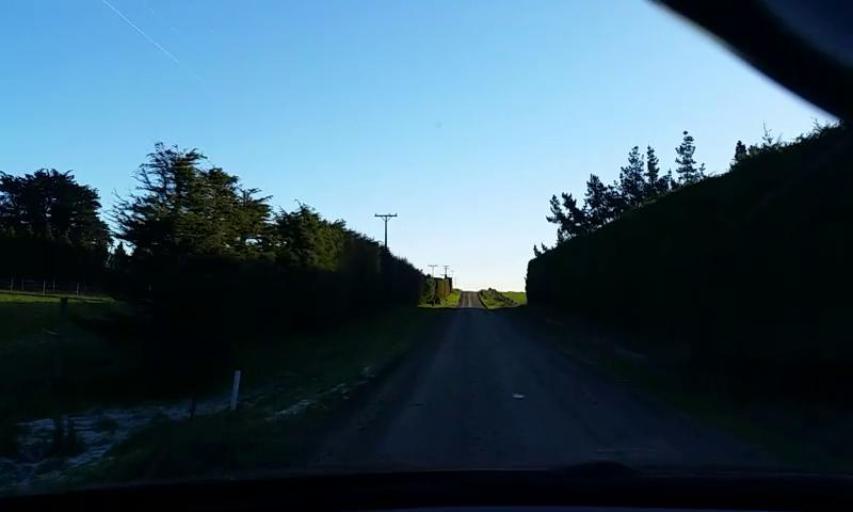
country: NZ
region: Southland
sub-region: Invercargill City
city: Invercargill
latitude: -46.2851
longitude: 168.4904
